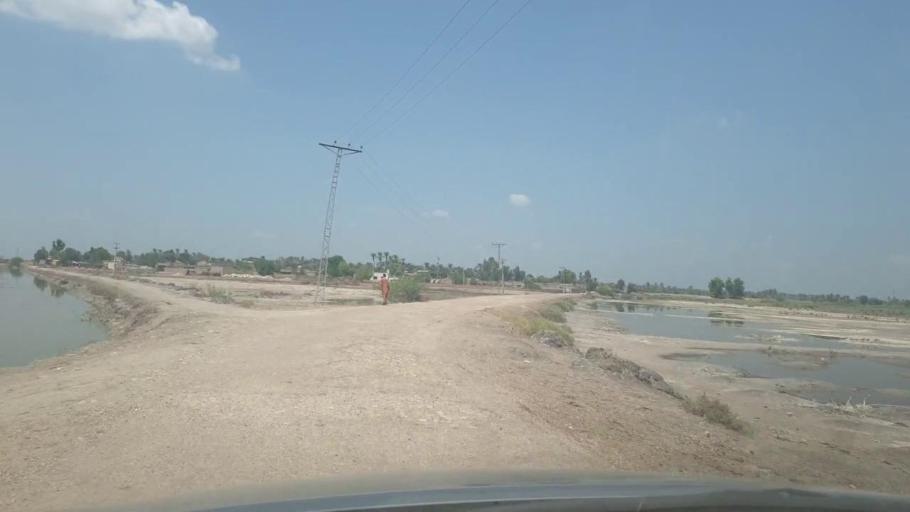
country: PK
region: Sindh
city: Kot Diji
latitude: 27.4177
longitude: 68.7361
